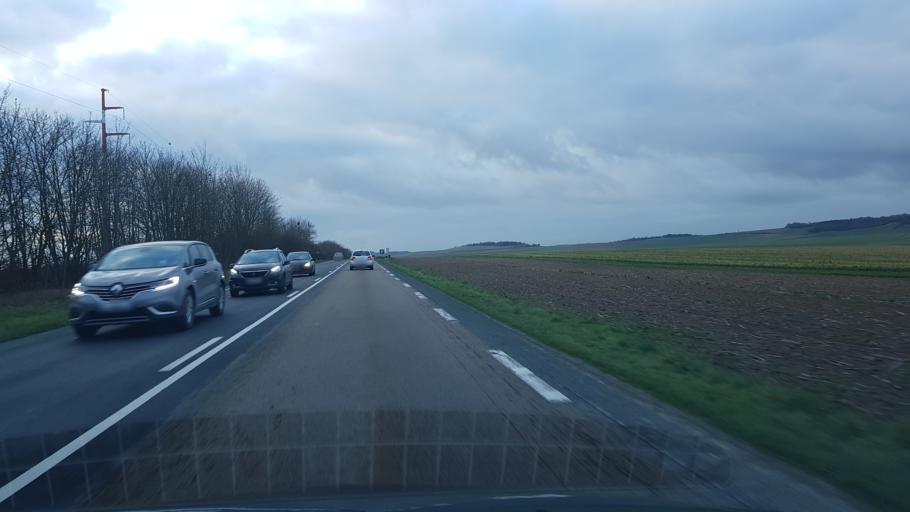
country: FR
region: Champagne-Ardenne
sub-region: Departement de la Marne
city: Sezanne
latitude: 48.7216
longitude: 3.7882
